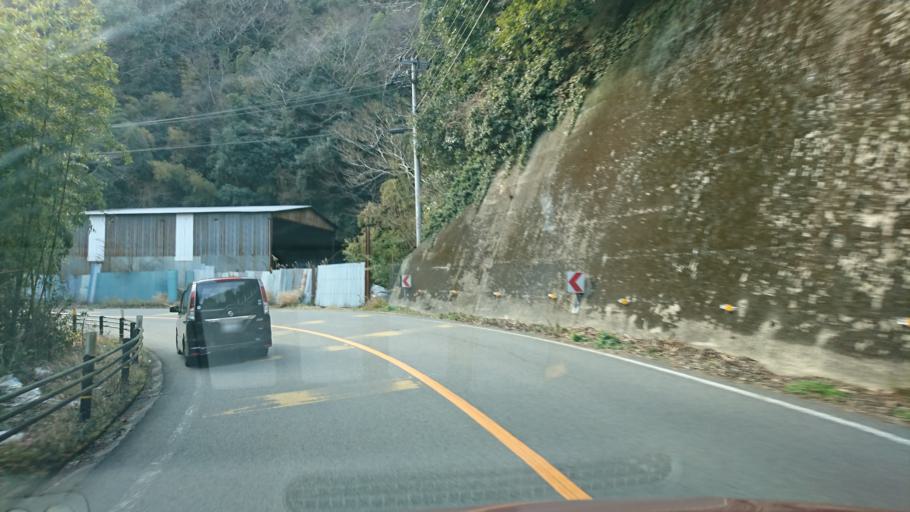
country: JP
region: Ehime
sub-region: Shikoku-chuo Shi
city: Matsuyama
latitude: 33.8931
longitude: 132.8409
